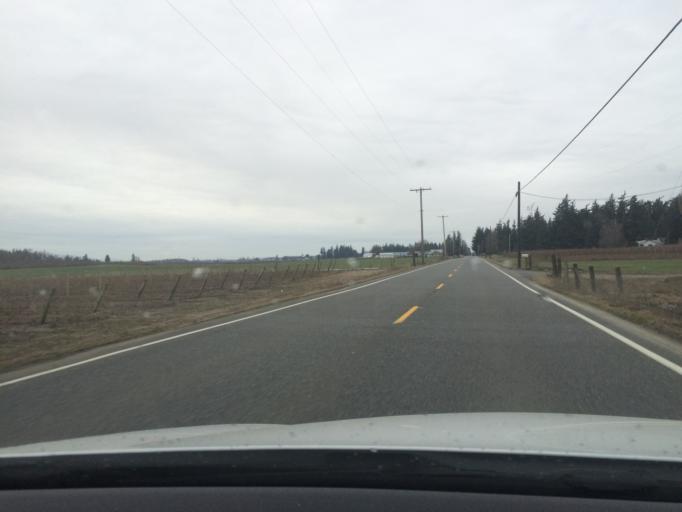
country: US
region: Washington
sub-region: Whatcom County
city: Lynden
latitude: 48.8916
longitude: -122.4160
